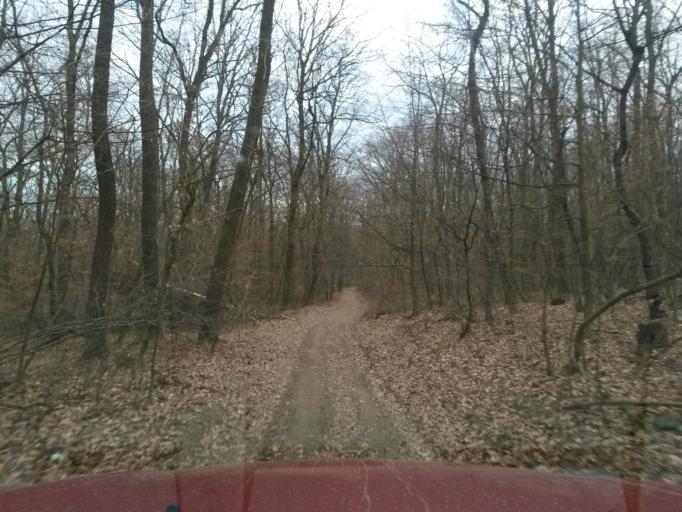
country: SK
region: Kosicky
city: Kosice
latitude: 48.7030
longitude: 21.2962
